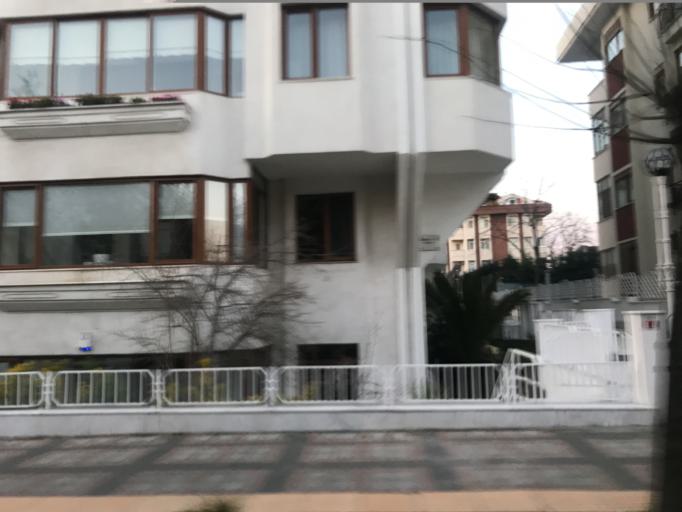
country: TR
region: Istanbul
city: Bahcelievler
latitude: 40.9610
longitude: 28.8257
